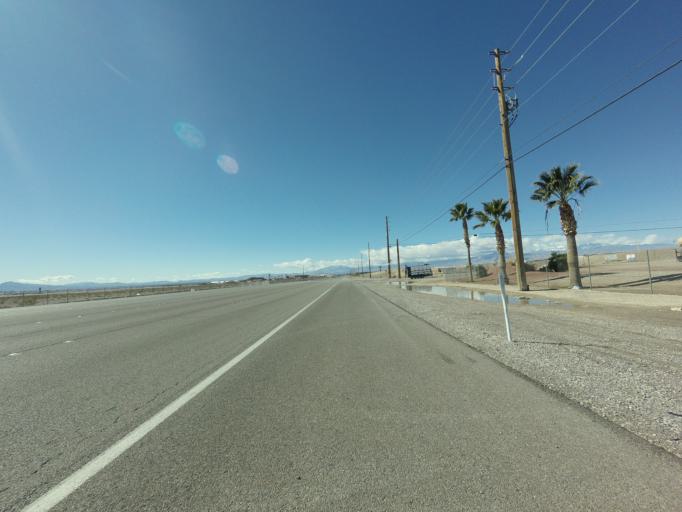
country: US
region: Nevada
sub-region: Clark County
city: Nellis Air Force Base
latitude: 36.2583
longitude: -115.0241
